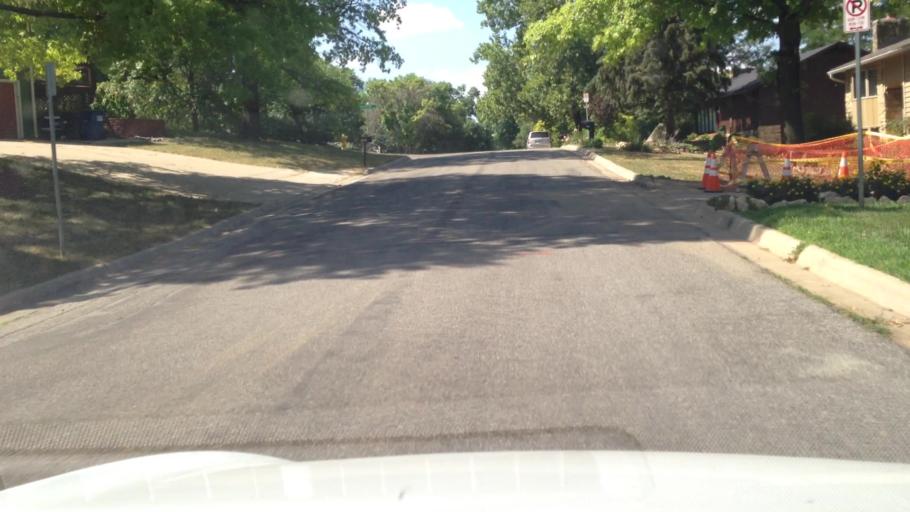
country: US
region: Kansas
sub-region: Douglas County
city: Lawrence
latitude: 38.9540
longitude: -95.2806
